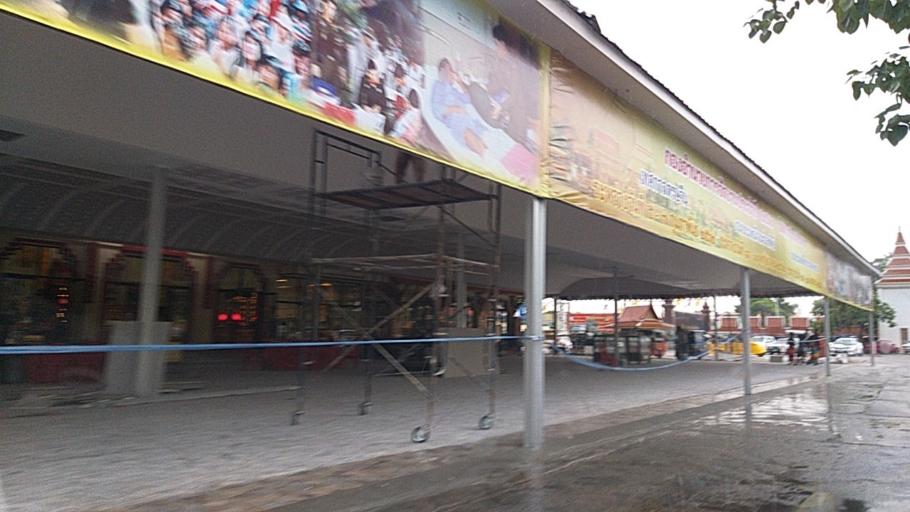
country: TH
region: Phra Nakhon Si Ayutthaya
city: Phra Nakhon Si Ayutthaya
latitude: 14.3444
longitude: 100.5798
